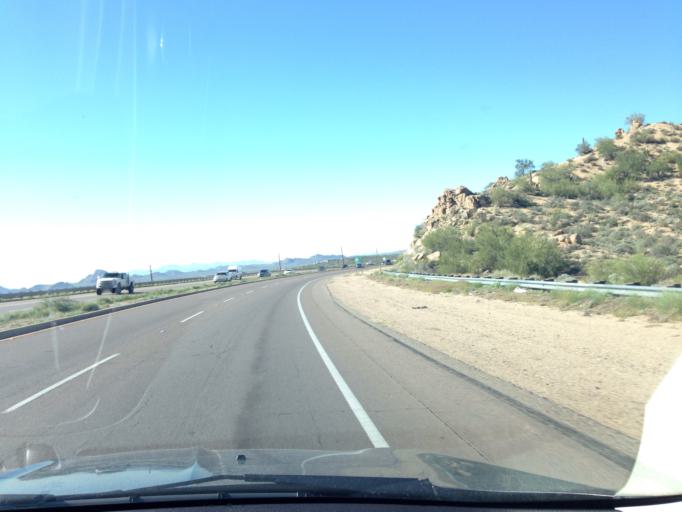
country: US
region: Arizona
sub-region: Maricopa County
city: Anthem
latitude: 33.7991
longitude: -112.0977
